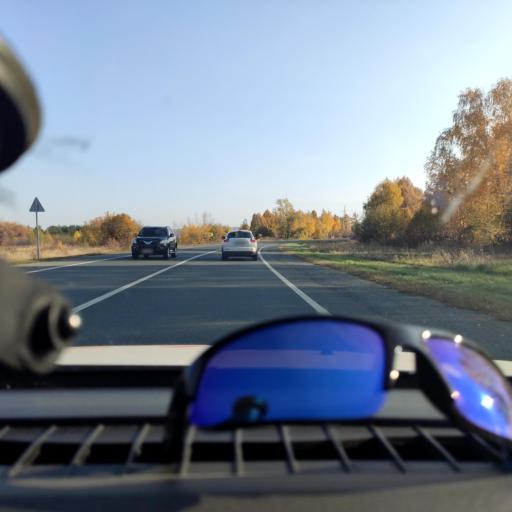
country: RU
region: Samara
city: Volzhskiy
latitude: 53.4670
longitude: 50.1268
